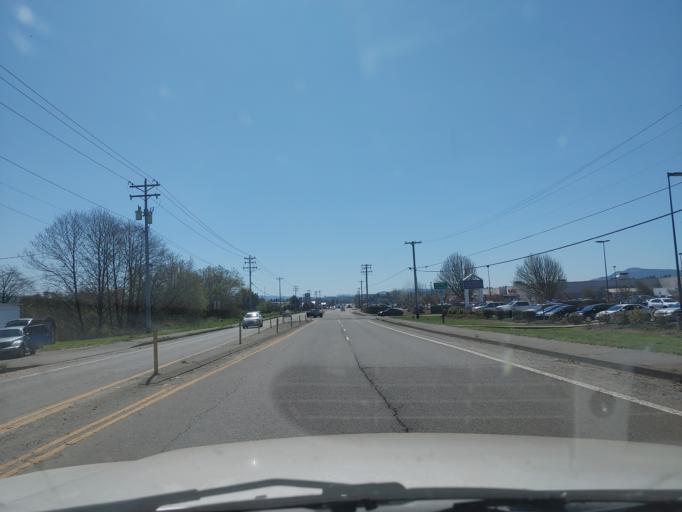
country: US
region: Oregon
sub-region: Tillamook County
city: Tillamook
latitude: 45.4775
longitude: -123.8445
